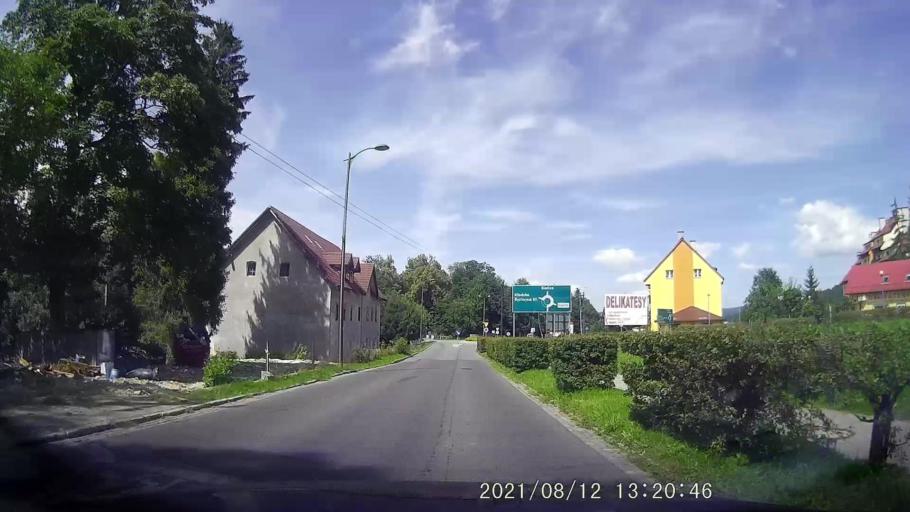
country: PL
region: Lower Silesian Voivodeship
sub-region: Powiat klodzki
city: Stronie Slaskie
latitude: 50.2902
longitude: 16.8757
